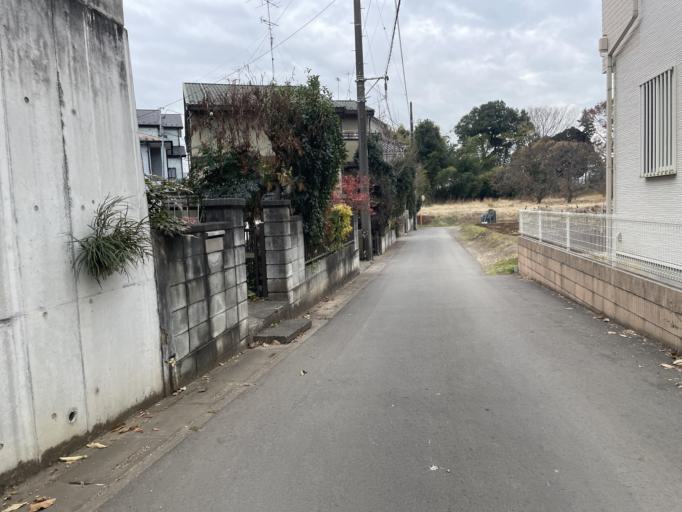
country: JP
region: Saitama
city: Shiraoka
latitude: 36.0013
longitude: 139.6602
